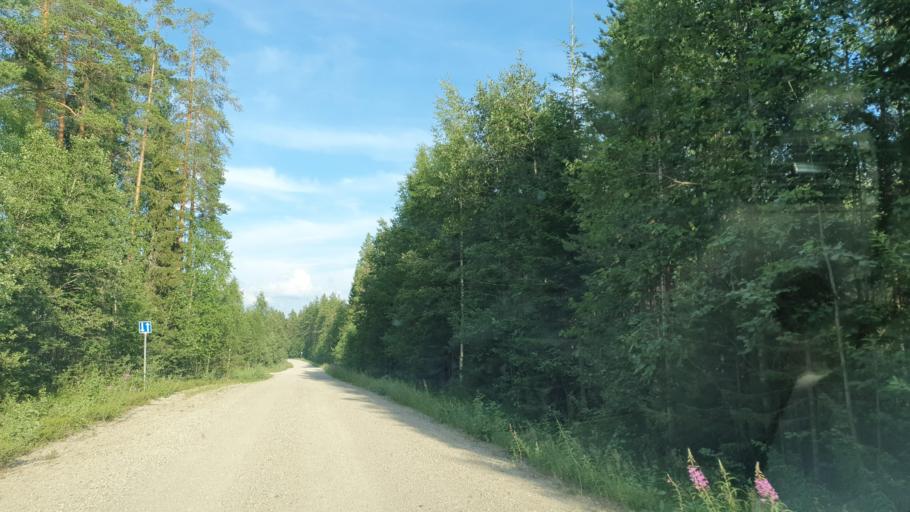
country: FI
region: Kainuu
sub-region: Kehys-Kainuu
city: Kuhmo
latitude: 64.2884
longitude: 29.7417
